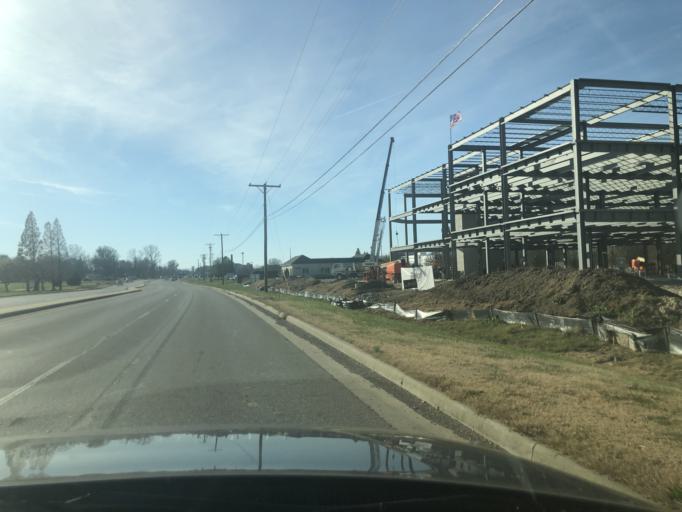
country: US
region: Indiana
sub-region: Warrick County
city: Newburgh
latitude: 37.9800
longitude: -87.4414
